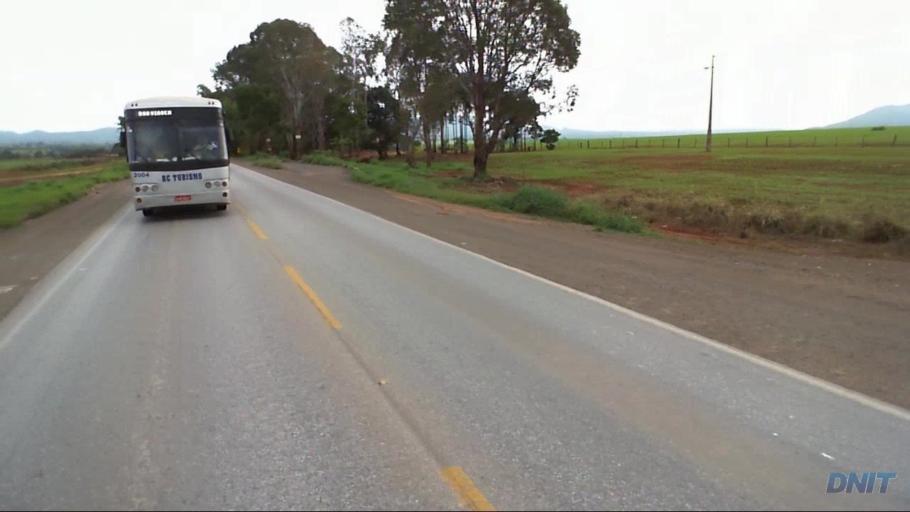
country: BR
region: Goias
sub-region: Uruacu
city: Uruacu
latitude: -14.6291
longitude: -49.1739
